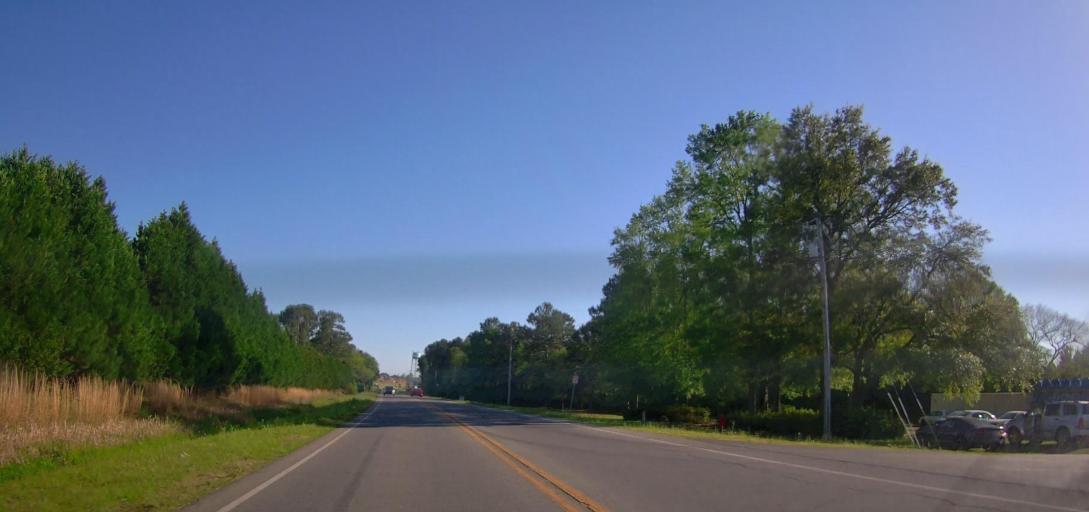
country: US
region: Georgia
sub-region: Ben Hill County
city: Fitzgerald
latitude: 31.7025
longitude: -83.2395
